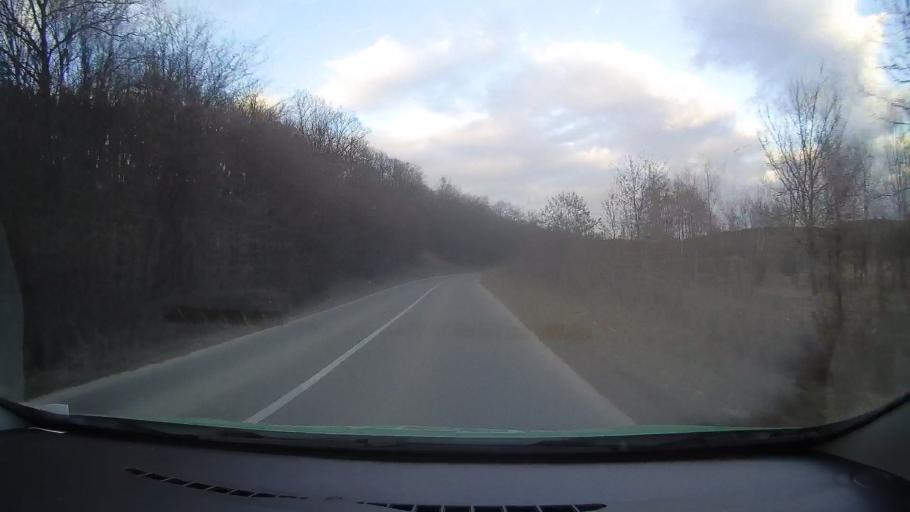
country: RO
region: Dambovita
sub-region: Comuna Gura Ocnitei
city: Gura Ocnitei
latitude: 44.9477
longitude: 25.5893
